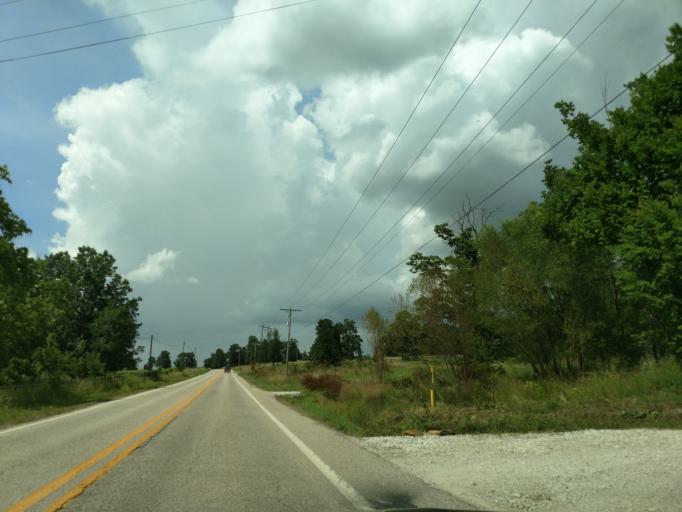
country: US
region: Arkansas
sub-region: Boone County
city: Harrison
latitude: 36.2627
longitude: -93.2302
